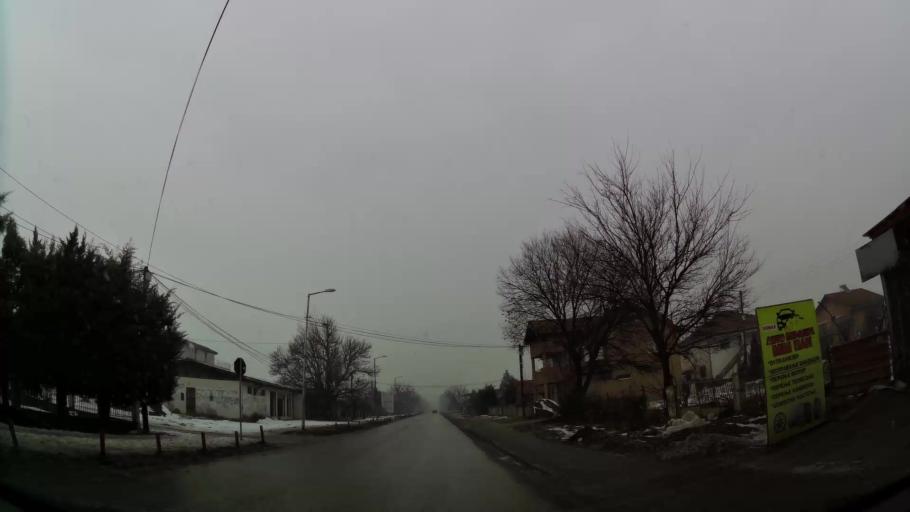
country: MK
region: Petrovec
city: Petrovec
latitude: 41.9274
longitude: 21.6287
